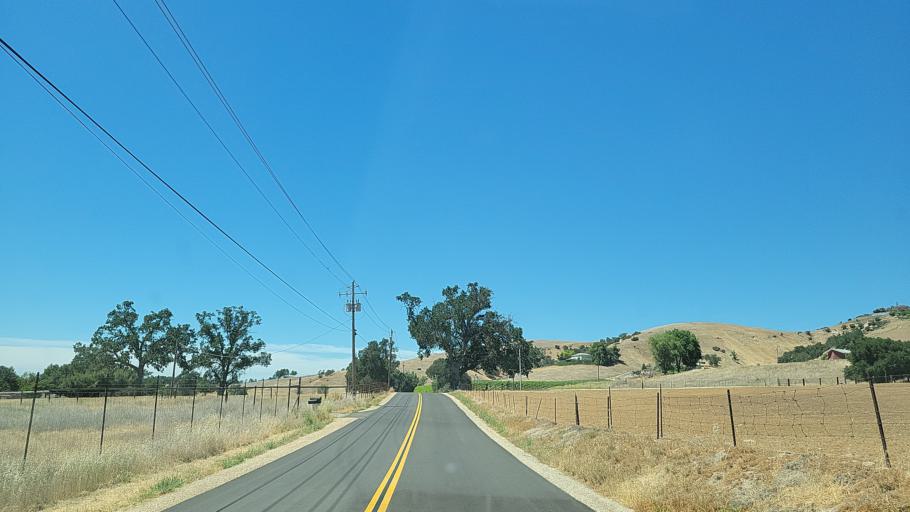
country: US
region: California
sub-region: San Luis Obispo County
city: Atascadero
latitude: 35.4841
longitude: -120.6319
